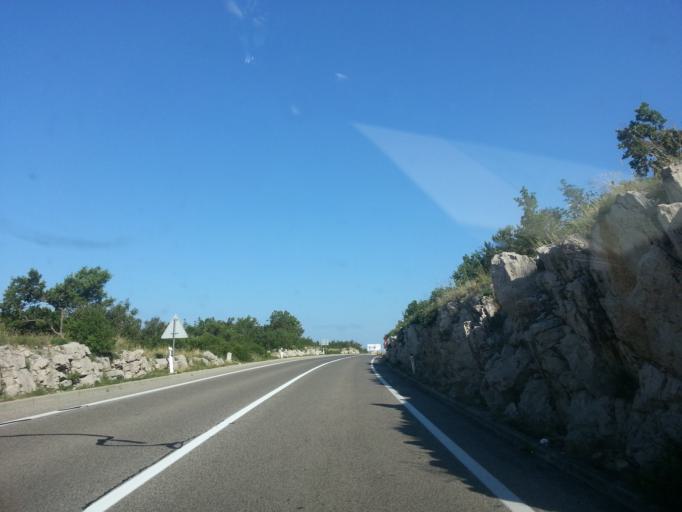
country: HR
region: Primorsko-Goranska
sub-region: Grad Crikvenica
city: Jadranovo
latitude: 45.2339
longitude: 14.6238
